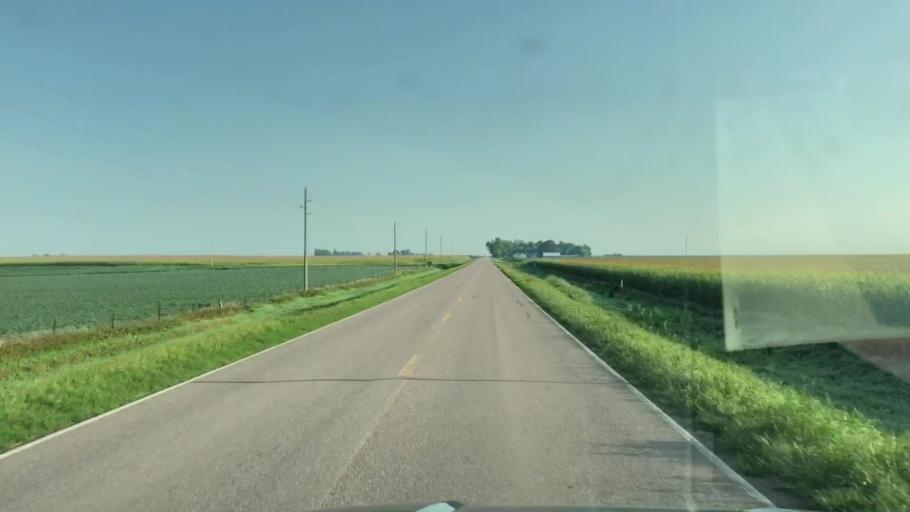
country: US
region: Iowa
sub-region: Sioux County
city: Hull
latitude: 43.1982
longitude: -96.0004
